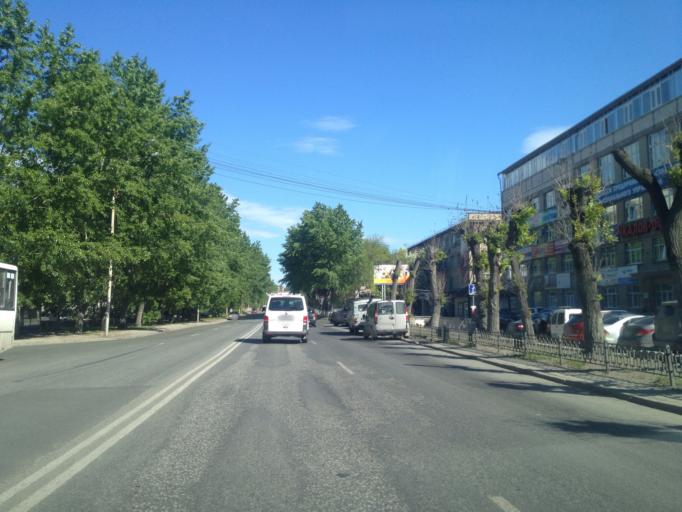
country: RU
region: Sverdlovsk
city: Yekaterinburg
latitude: 56.8252
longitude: 60.6446
